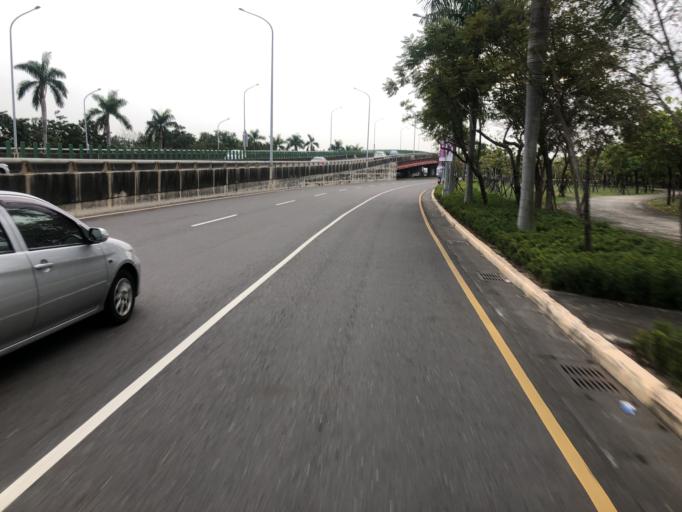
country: TW
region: Taiwan
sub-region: Tainan
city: Tainan
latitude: 23.0873
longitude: 120.2825
